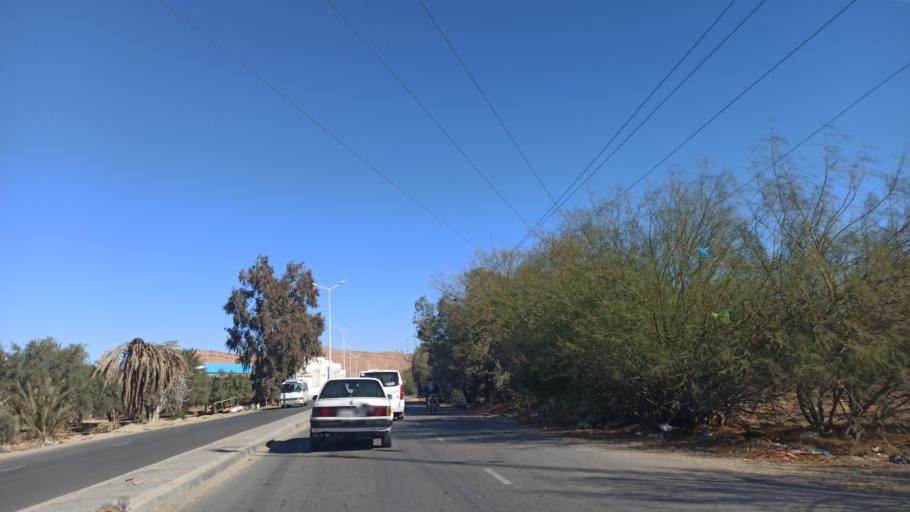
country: TN
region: Gafsa
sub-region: Gafsa Municipality
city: Gafsa
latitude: 34.4195
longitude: 8.7449
